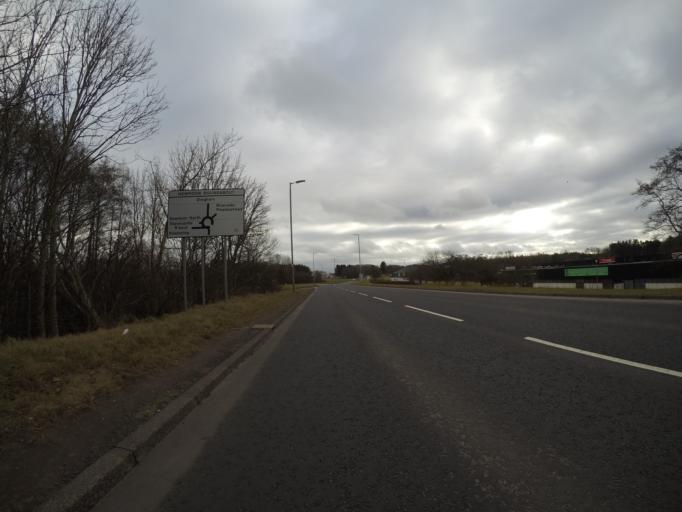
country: GB
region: Scotland
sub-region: North Ayrshire
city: Irvine
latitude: 55.6093
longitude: -4.6434
